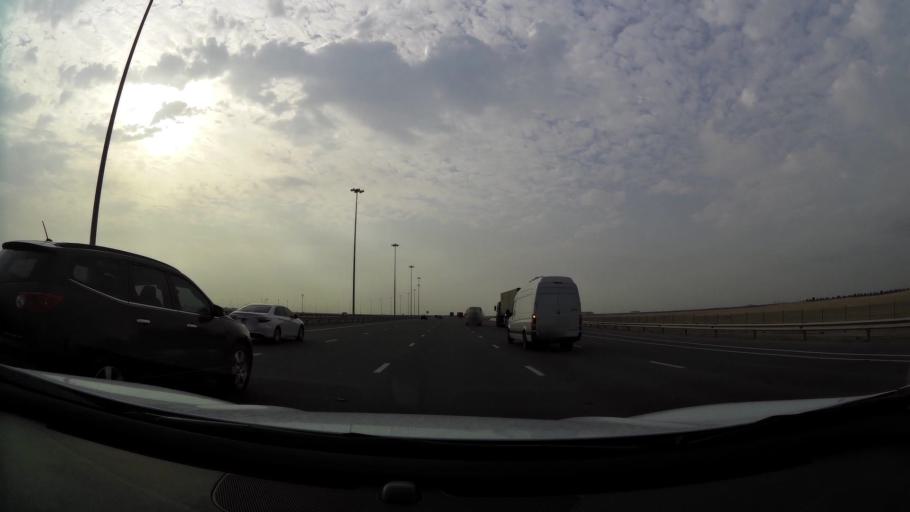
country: AE
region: Abu Dhabi
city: Abu Dhabi
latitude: 24.5378
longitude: 54.4846
